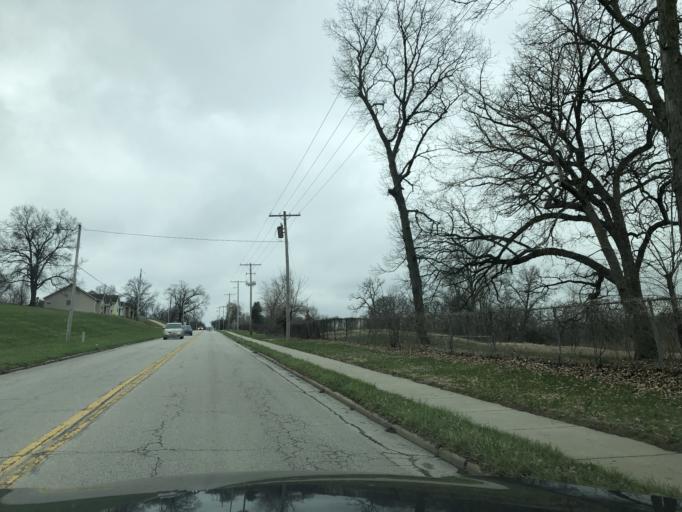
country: US
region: Kansas
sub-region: Leavenworth County
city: Leavenworth
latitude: 39.2831
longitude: -94.9185
